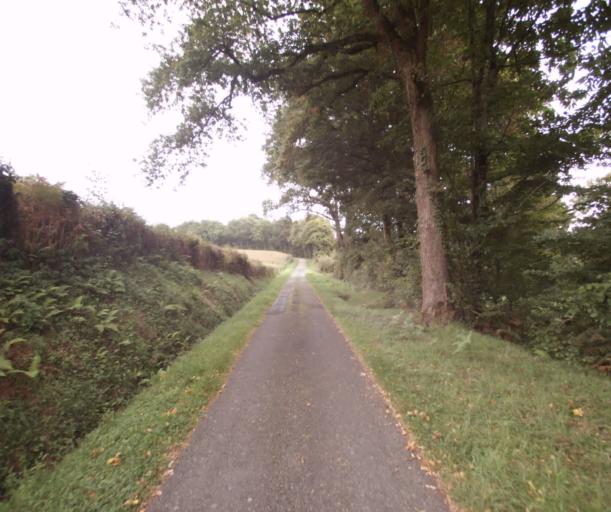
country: FR
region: Midi-Pyrenees
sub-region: Departement du Gers
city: Cazaubon
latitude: 43.8722
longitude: -0.0799
